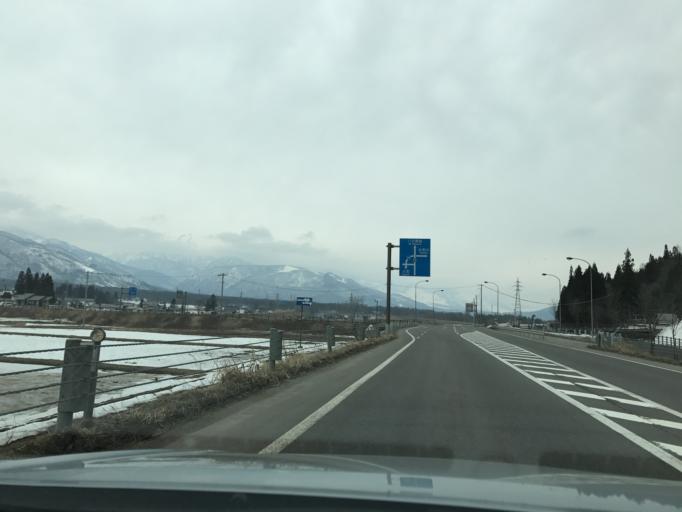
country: JP
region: Nagano
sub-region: Kitaazumi Gun
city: Hakuba
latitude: 36.6666
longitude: 137.8515
